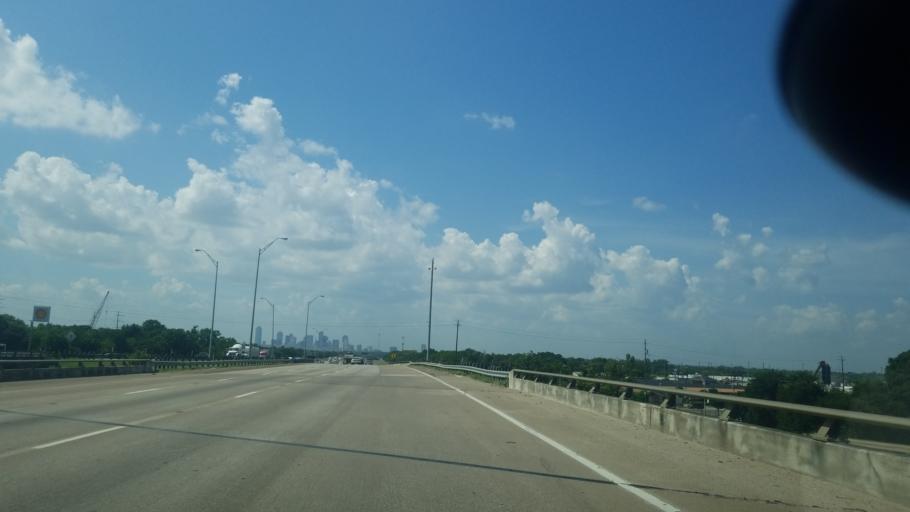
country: US
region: Texas
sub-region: Dallas County
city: Hutchins
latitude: 32.7134
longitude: -96.7564
